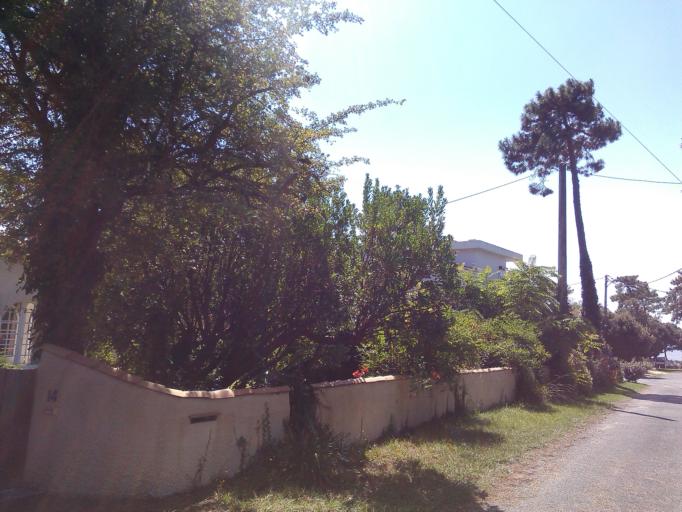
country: FR
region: Poitou-Charentes
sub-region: Departement de la Charente-Maritime
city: Vaux-sur-Mer
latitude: 45.6360
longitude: -1.0722
